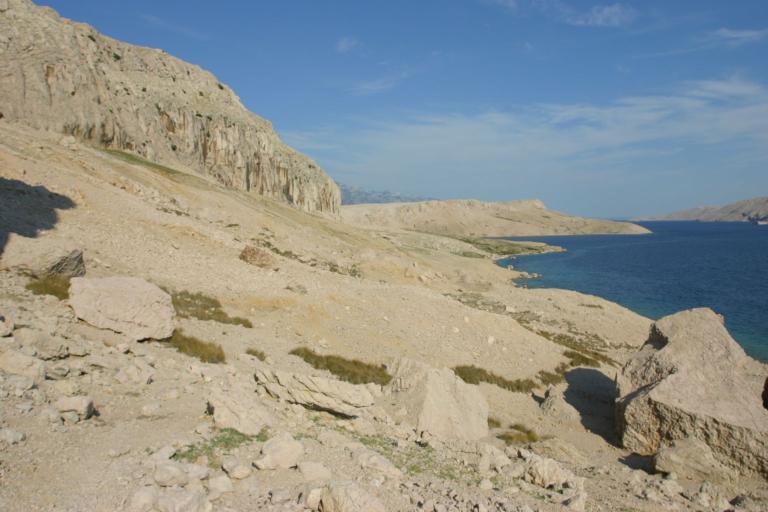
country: HR
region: Licko-Senjska
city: Karlobag
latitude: 44.4995
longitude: 15.0335
